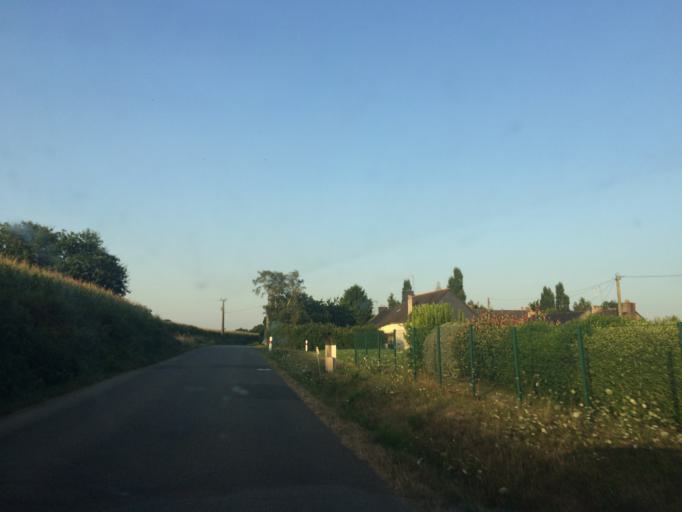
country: FR
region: Brittany
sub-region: Departement du Morbihan
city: Allaire
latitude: 47.6351
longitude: -2.1913
